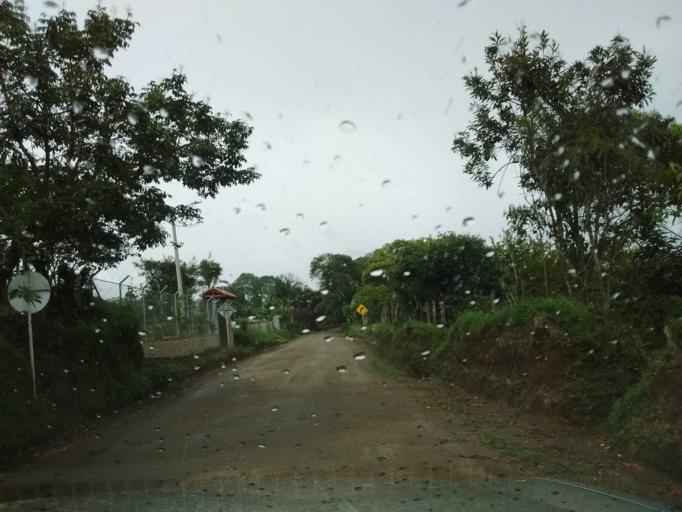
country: CO
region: Cauca
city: Popayan
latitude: 2.5246
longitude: -76.5952
